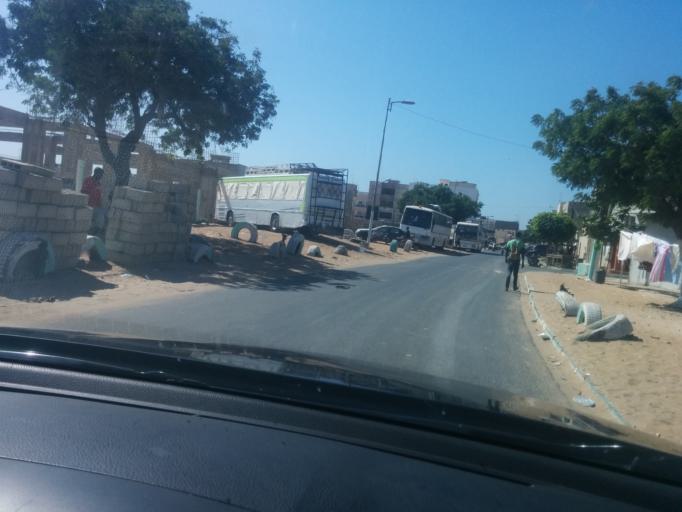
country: SN
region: Dakar
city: Grand Dakar
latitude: 14.7408
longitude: -17.4410
